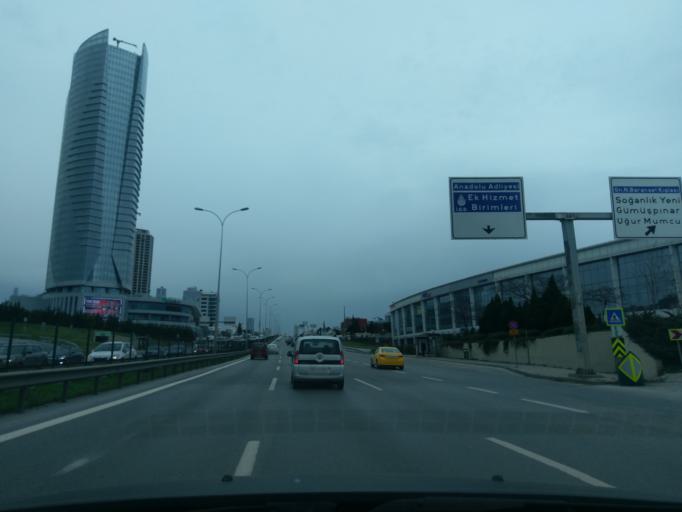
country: TR
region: Istanbul
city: Maltepe
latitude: 40.9188
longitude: 29.1717
